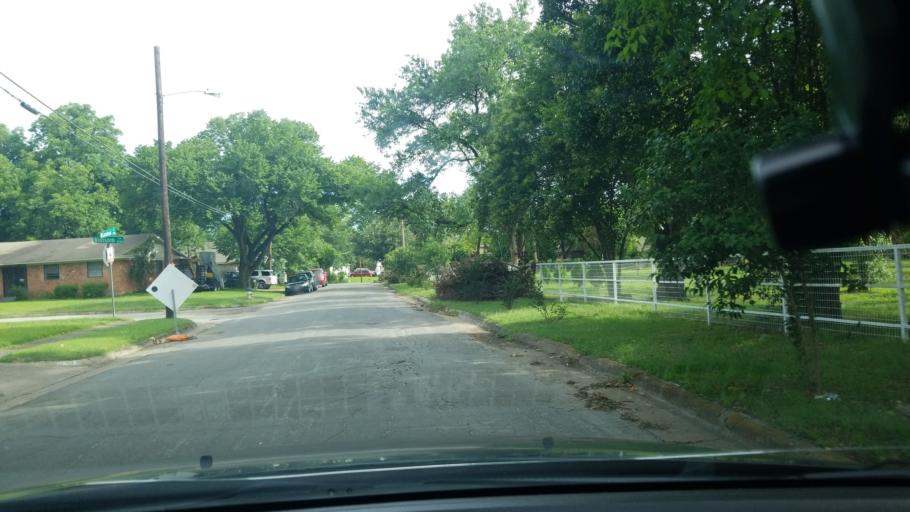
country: US
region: Texas
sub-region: Dallas County
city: Balch Springs
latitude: 32.7584
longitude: -96.6694
